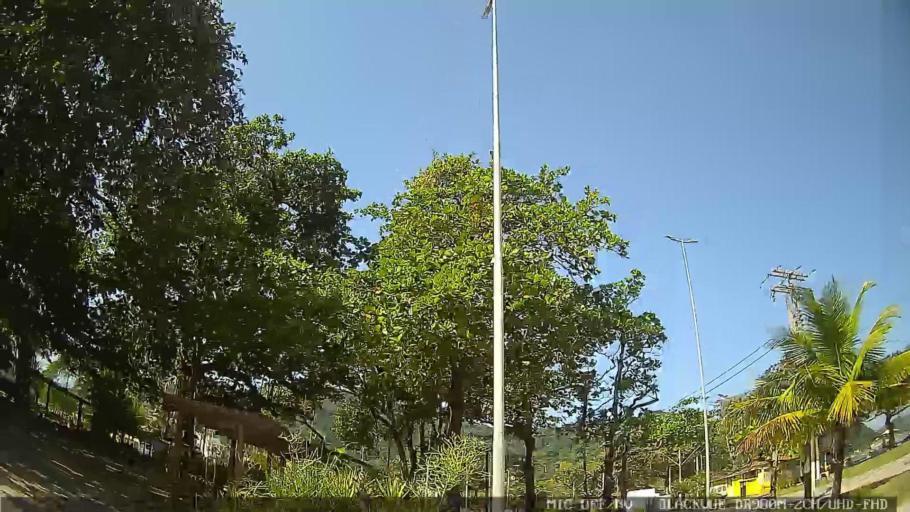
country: BR
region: Sao Paulo
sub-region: Guaruja
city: Guaruja
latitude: -24.0198
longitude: -46.2985
